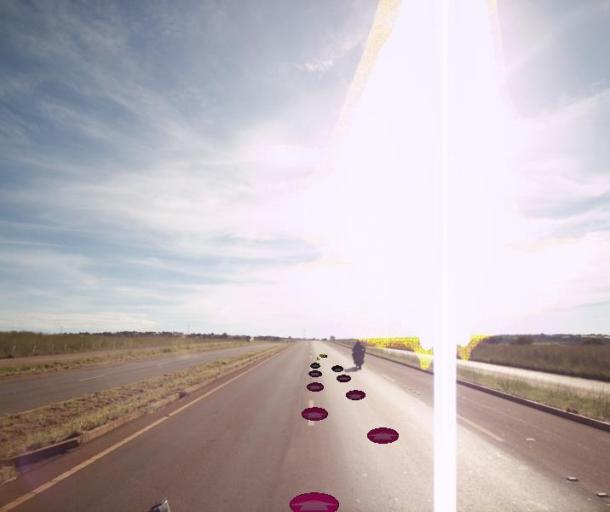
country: BR
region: Federal District
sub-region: Brasilia
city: Brasilia
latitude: -15.7465
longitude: -48.3198
